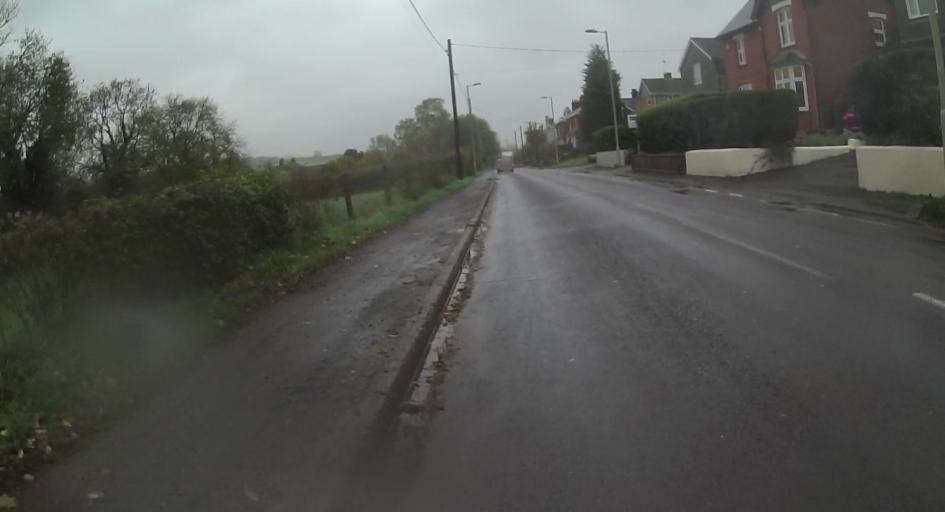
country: GB
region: England
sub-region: Hampshire
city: Alton
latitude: 51.1461
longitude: -0.9937
